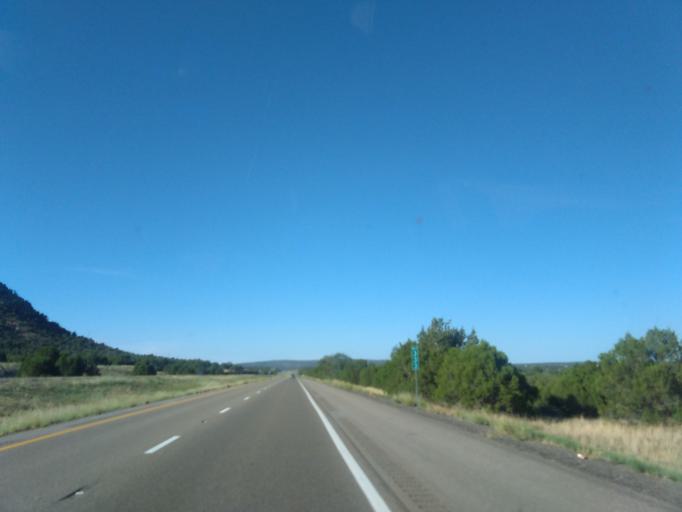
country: US
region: New Mexico
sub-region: San Miguel County
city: Las Vegas
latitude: 35.4290
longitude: -105.2956
